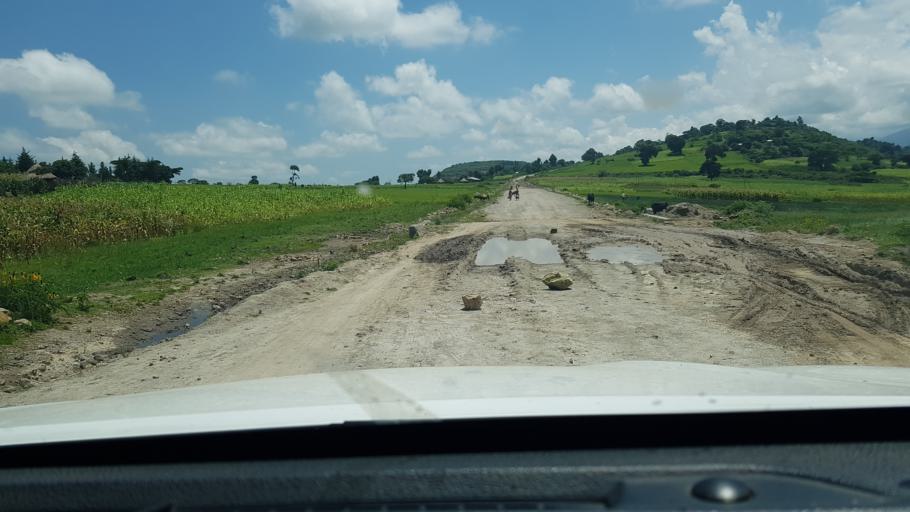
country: ET
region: Oromiya
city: Sirre
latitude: 8.4375
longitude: 39.8777
